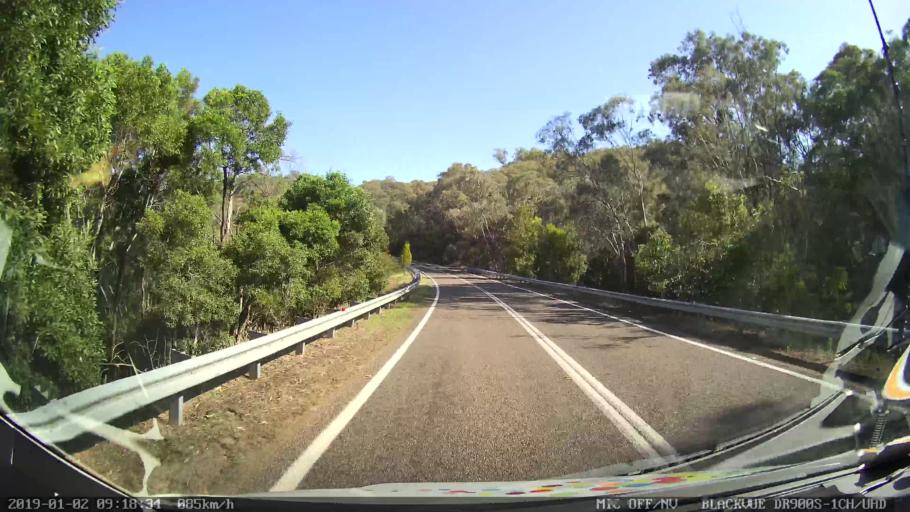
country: AU
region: New South Wales
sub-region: Tumut Shire
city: Tumut
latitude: -35.4275
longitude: 148.2872
